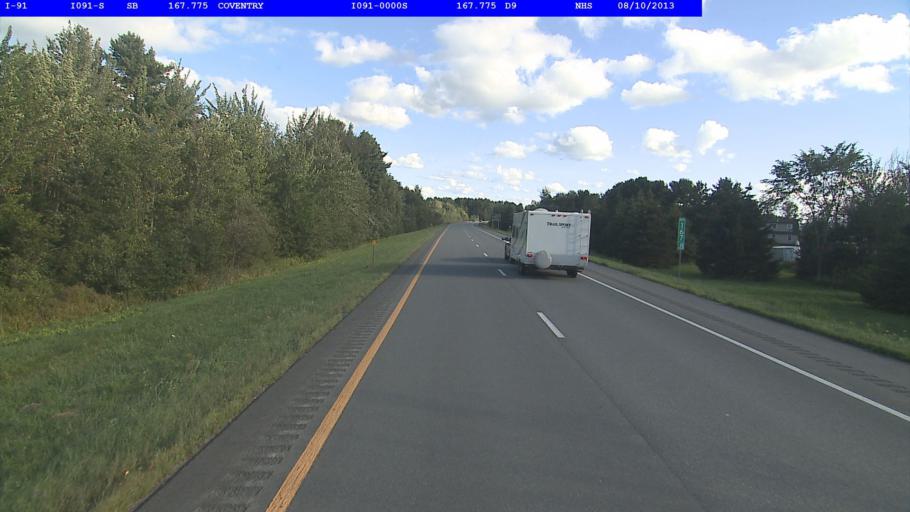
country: US
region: Vermont
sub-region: Orleans County
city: Newport
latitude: 44.8908
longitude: -72.1734
